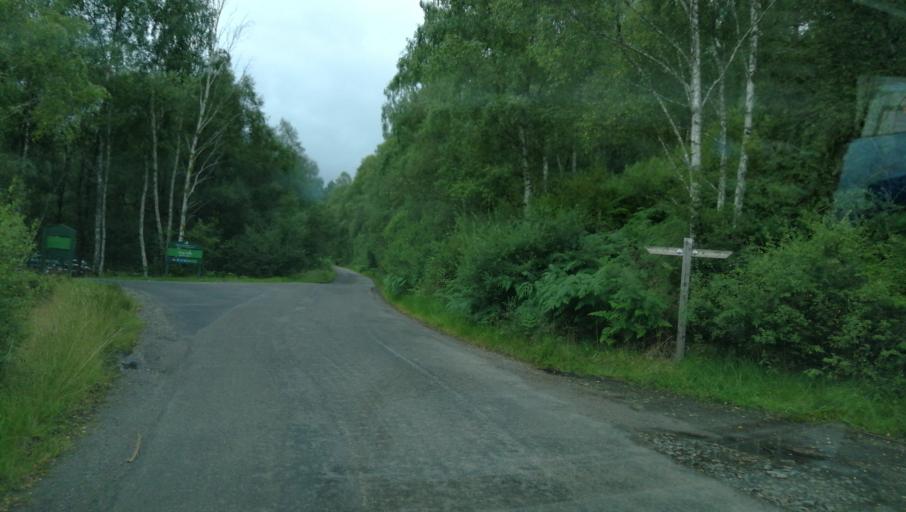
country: GB
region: Scotland
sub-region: Highland
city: Beauly
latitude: 57.3128
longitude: -4.8513
